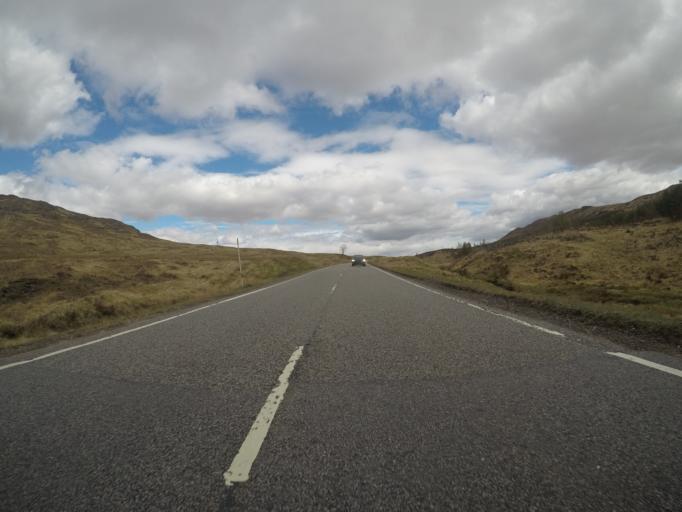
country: GB
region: Scotland
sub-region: Highland
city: Spean Bridge
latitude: 56.5794
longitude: -4.7555
